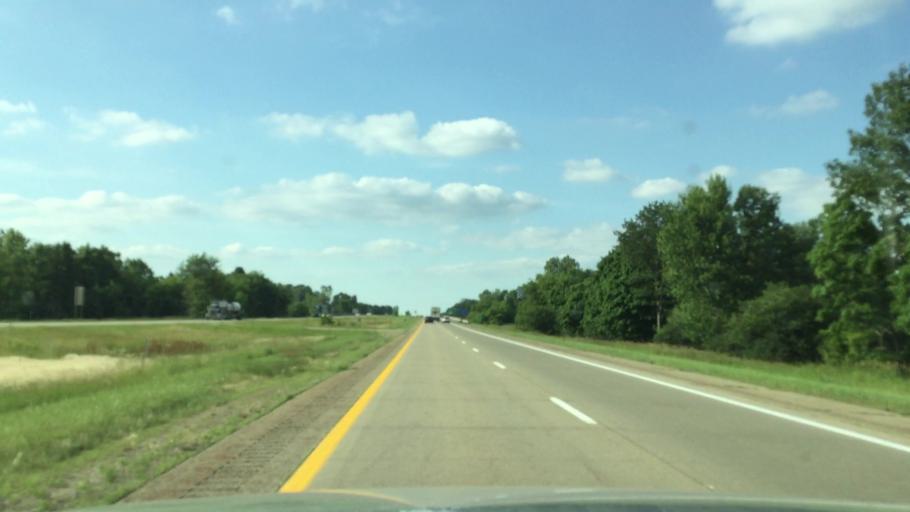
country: US
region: Michigan
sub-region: Branch County
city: Union City
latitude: 42.0934
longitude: -84.9972
